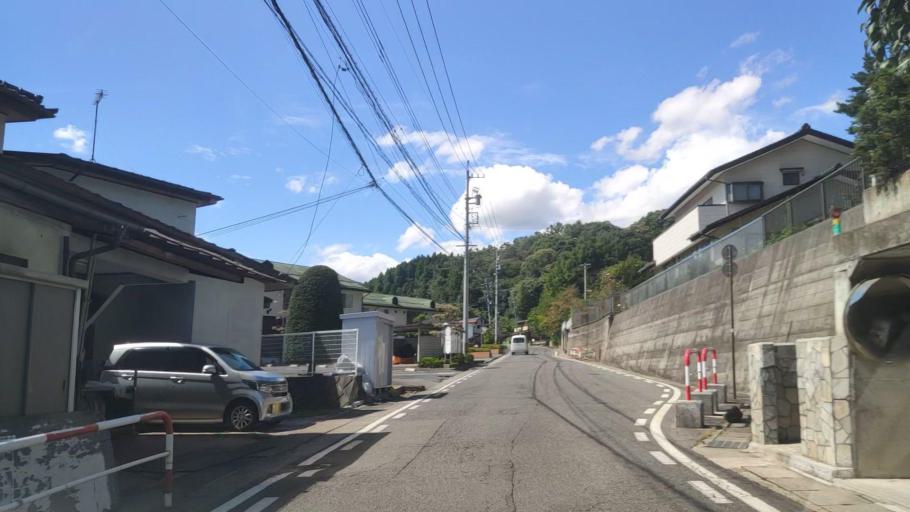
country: JP
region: Nagano
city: Nagano-shi
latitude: 36.6869
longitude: 138.2094
